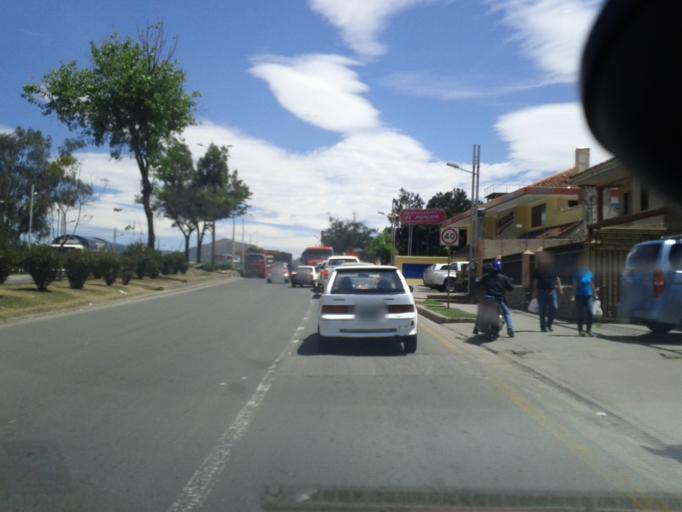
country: EC
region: Azuay
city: Cuenca
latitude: -2.8930
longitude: -79.0250
